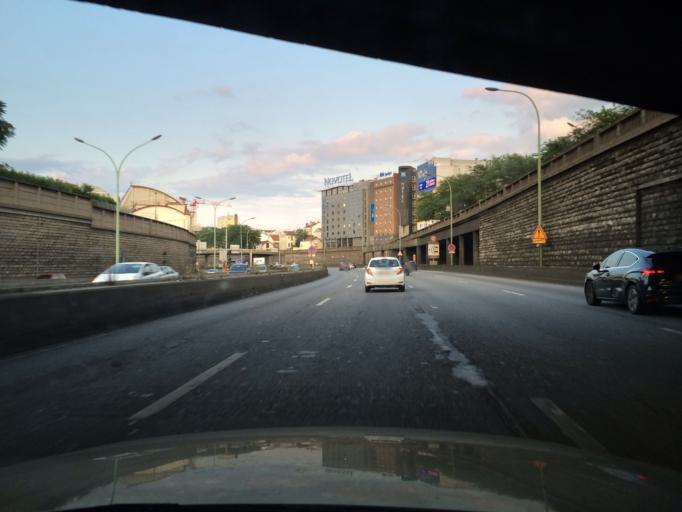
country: FR
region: Ile-de-France
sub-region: Departement du Val-de-Marne
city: Le Kremlin-Bicetre
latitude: 48.8160
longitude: 2.3611
